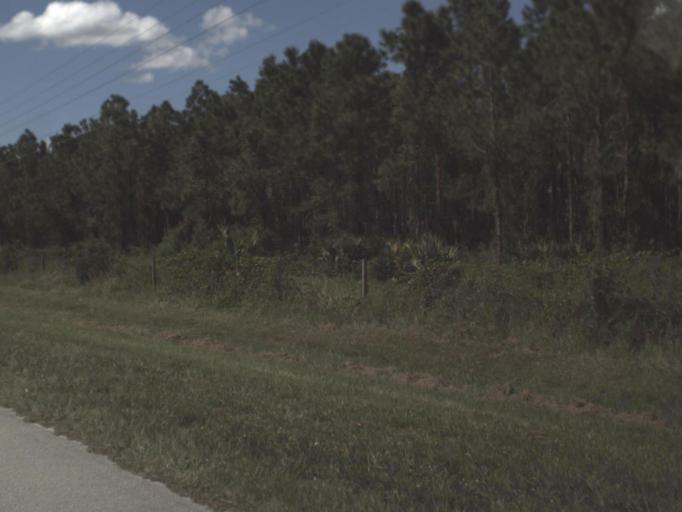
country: US
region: Florida
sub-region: Hendry County
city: Port LaBelle
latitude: 26.8125
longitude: -81.2760
